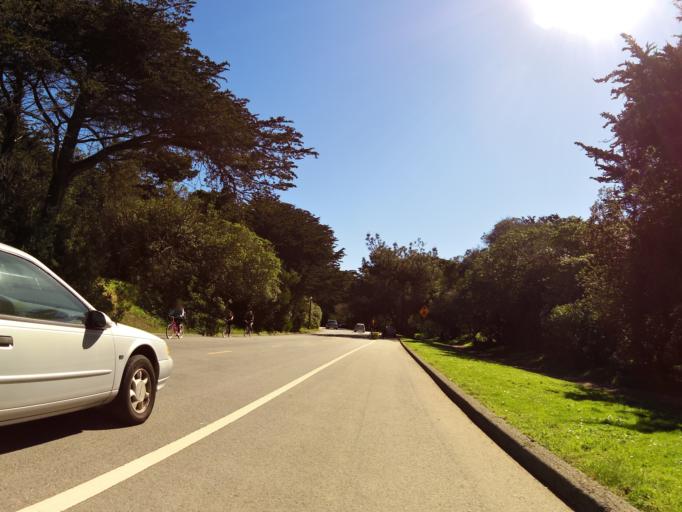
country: US
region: California
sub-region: San Mateo County
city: Daly City
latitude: 37.7678
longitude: -122.5073
